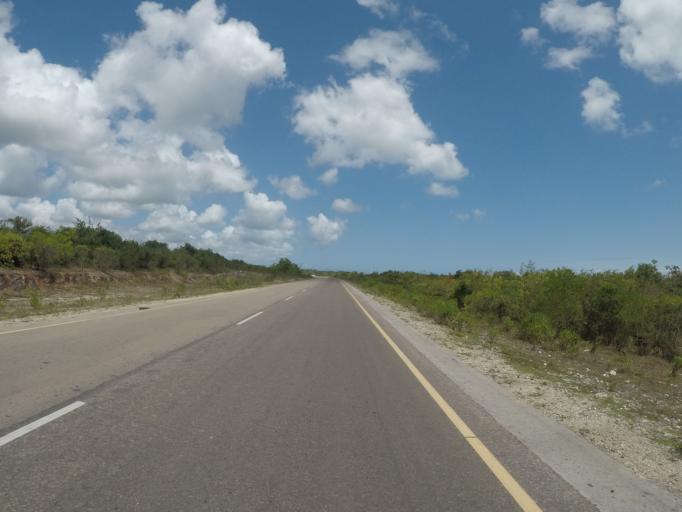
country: TZ
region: Zanzibar Central/South
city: Koani
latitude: -6.2744
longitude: 39.3643
